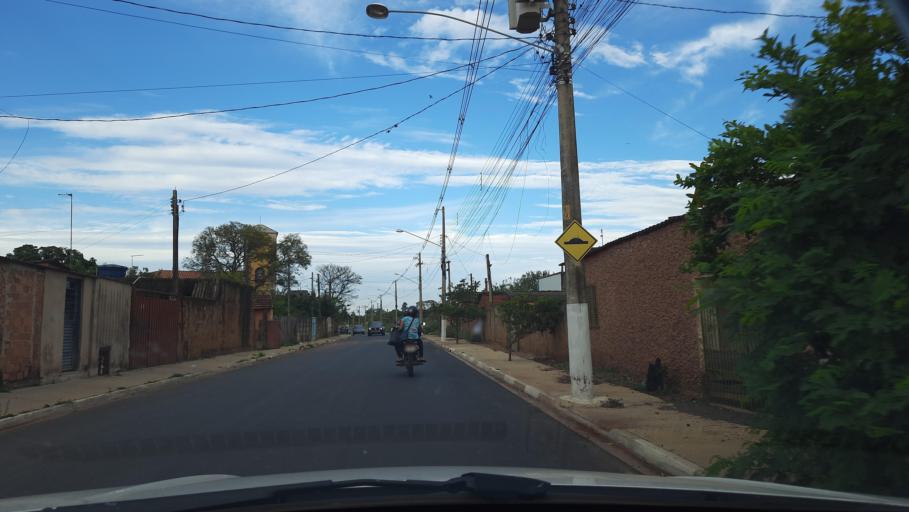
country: BR
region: Sao Paulo
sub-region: Casa Branca
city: Casa Branca
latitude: -21.7607
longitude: -47.0845
